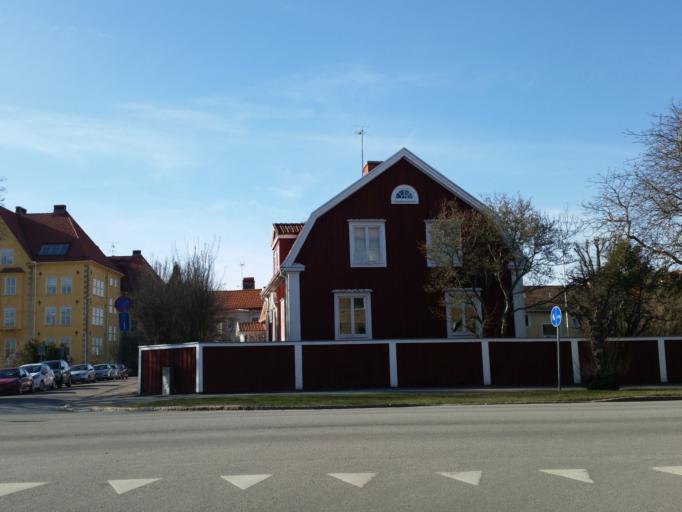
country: SE
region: Kalmar
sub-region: Kalmar Kommun
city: Kalmar
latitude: 56.6613
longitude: 16.3458
